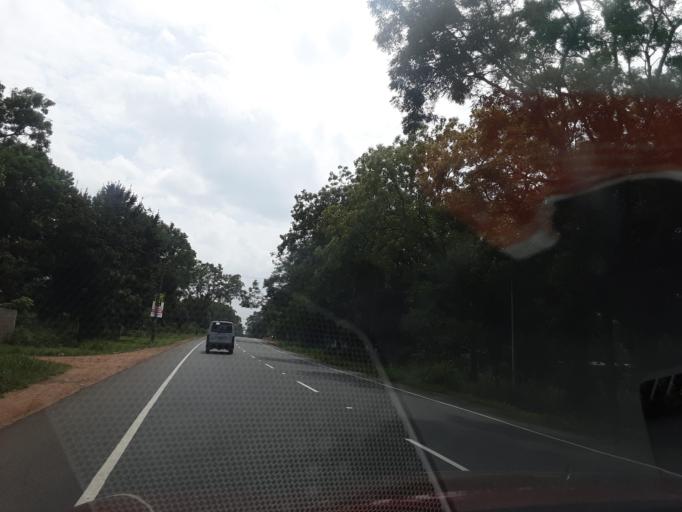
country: LK
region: North Central
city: Anuradhapura
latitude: 8.4921
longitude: 80.5118
